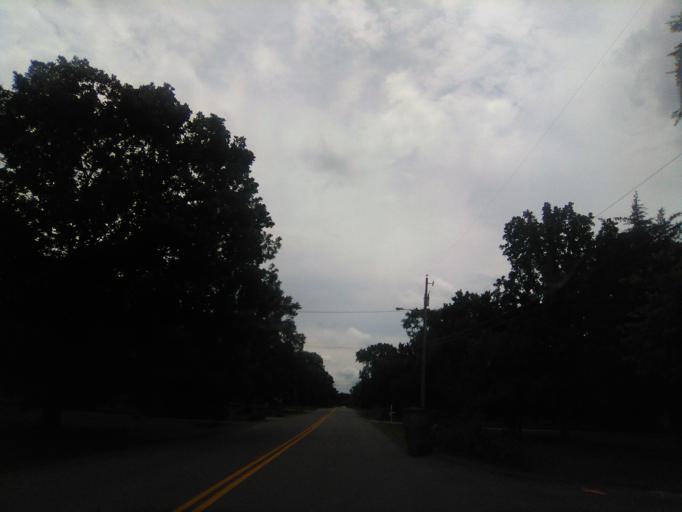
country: US
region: Tennessee
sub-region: Davidson County
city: Belle Meade
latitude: 36.1270
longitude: -86.8919
